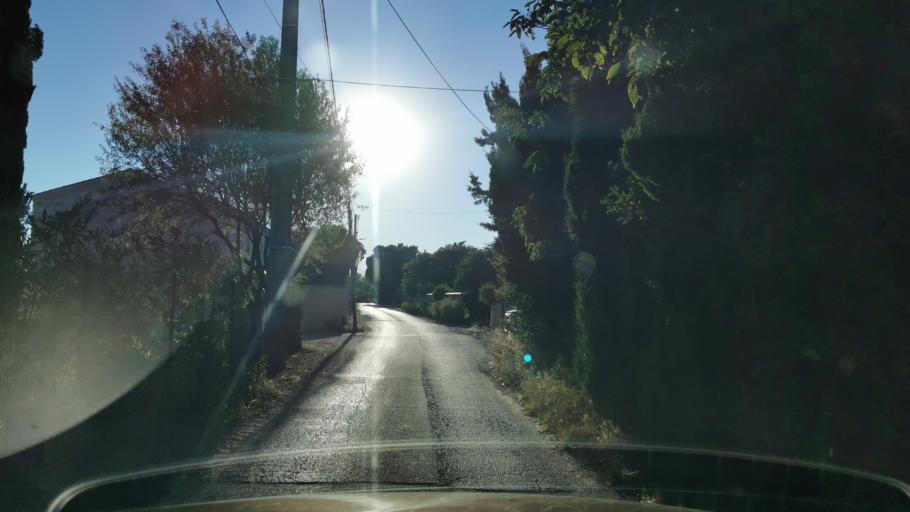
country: FR
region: Languedoc-Roussillon
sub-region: Departement de l'Aude
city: Ouveillan
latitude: 43.2681
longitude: 3.0151
